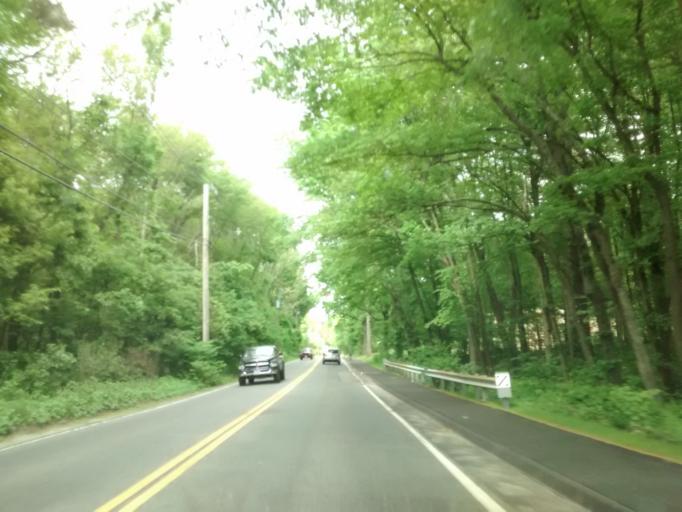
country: US
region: Massachusetts
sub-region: Middlesex County
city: Hopkinton
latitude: 42.2210
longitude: -71.5359
